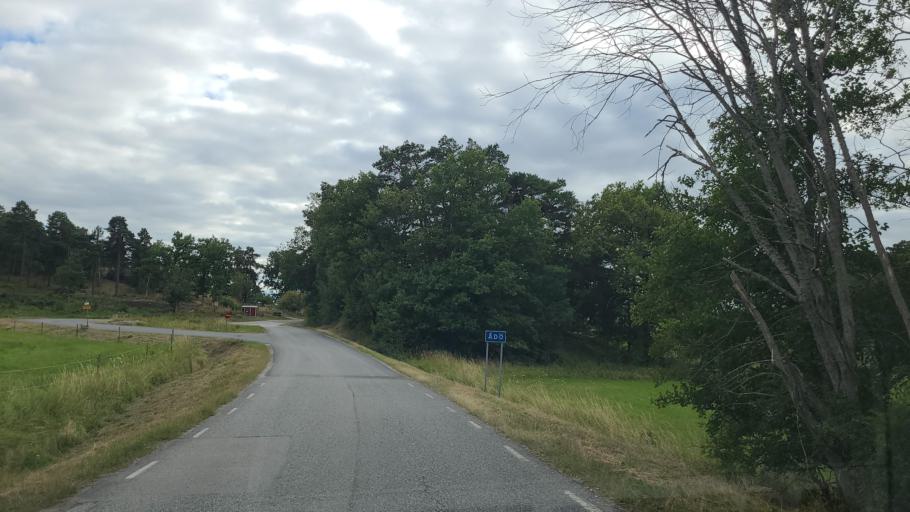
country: SE
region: Stockholm
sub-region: Upplands-Bro Kommun
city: Bro
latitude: 59.4688
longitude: 17.5921
